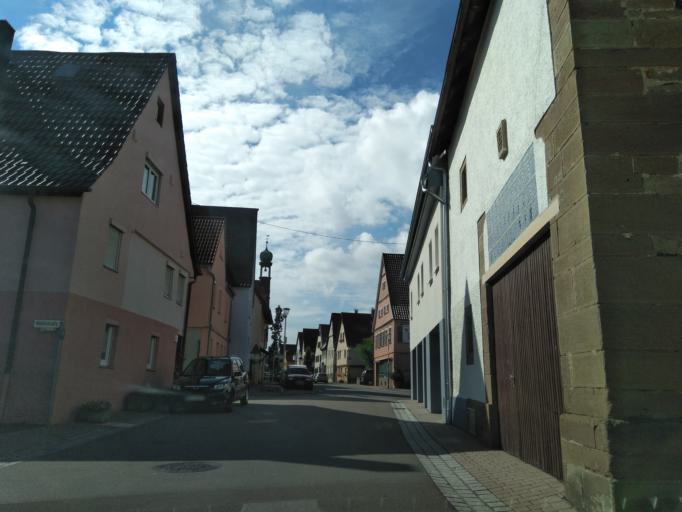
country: DE
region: Baden-Wuerttemberg
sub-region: Regierungsbezirk Stuttgart
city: Walheim
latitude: 49.0117
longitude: 9.1553
